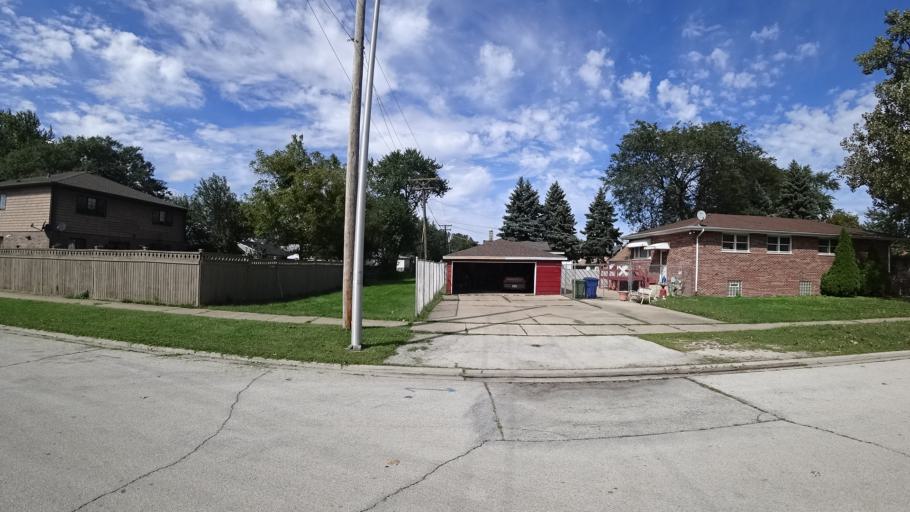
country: US
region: Illinois
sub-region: Cook County
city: Chicago Ridge
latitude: 41.7087
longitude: -87.7752
